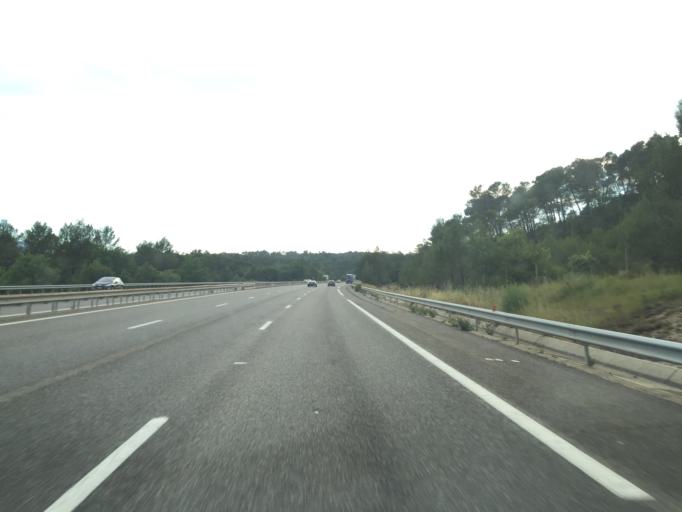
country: FR
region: Provence-Alpes-Cote d'Azur
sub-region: Departement du Var
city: Tourves
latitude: 43.4241
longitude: 5.9673
